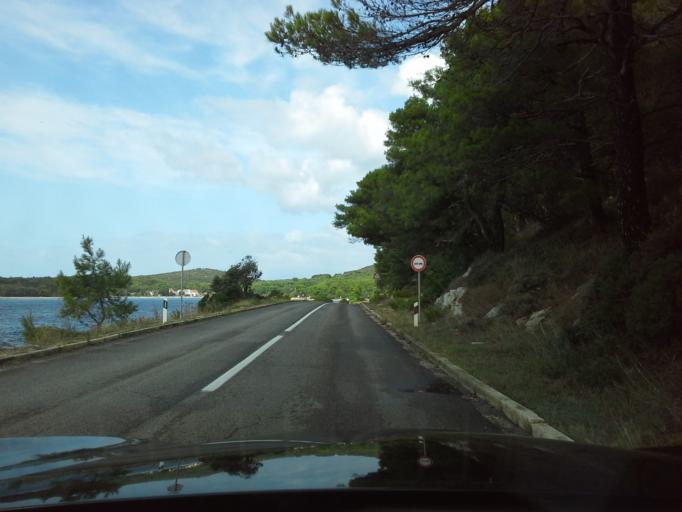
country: HR
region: Primorsko-Goranska
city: Mali Losinj
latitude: 44.5620
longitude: 14.4357
